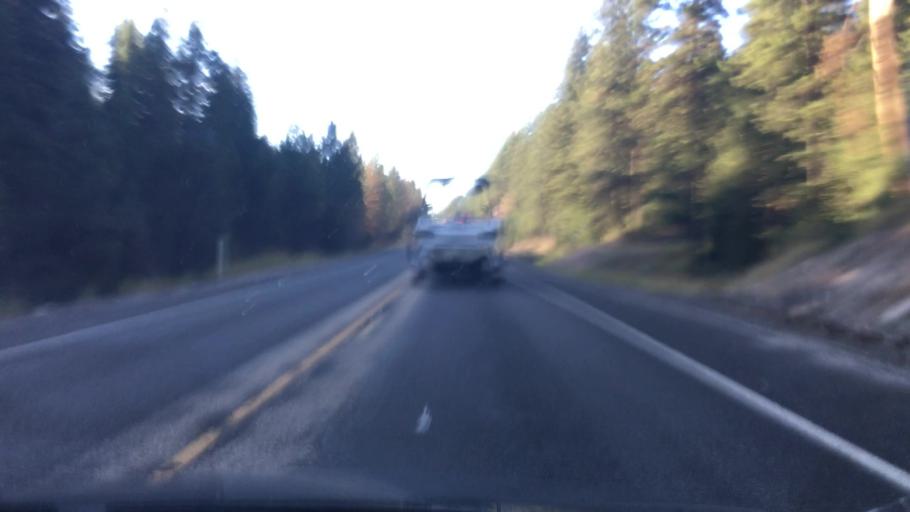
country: US
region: Idaho
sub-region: Valley County
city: Cascade
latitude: 44.5704
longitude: -116.0303
